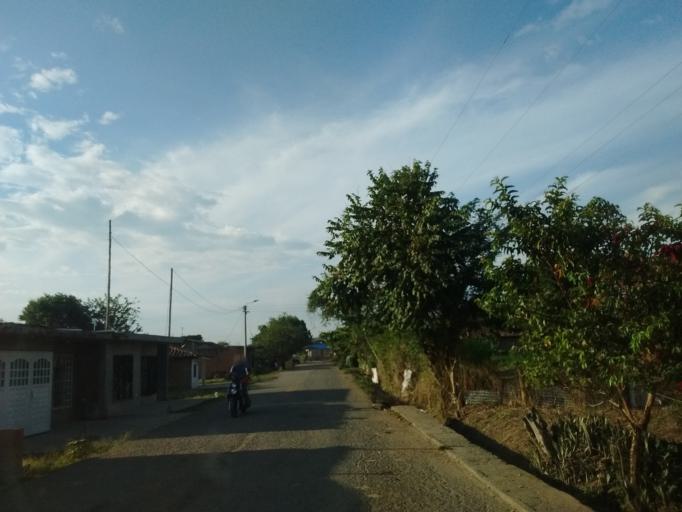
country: CO
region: Cauca
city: Puerto Tejada
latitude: 3.2189
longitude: -76.4435
